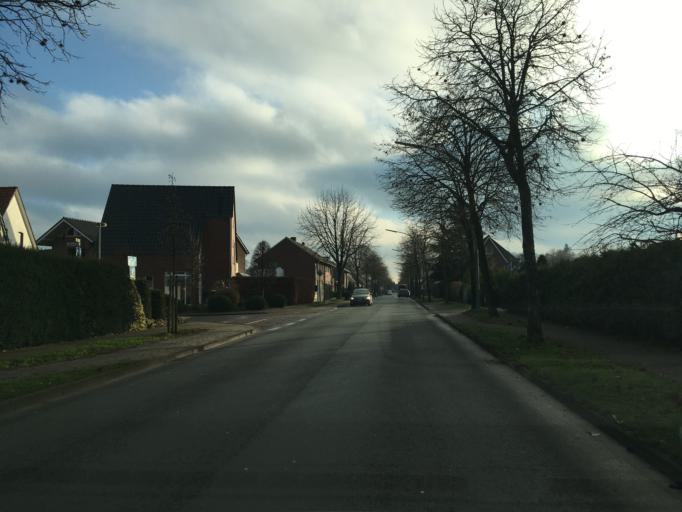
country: DE
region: North Rhine-Westphalia
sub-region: Regierungsbezirk Munster
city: Gescher
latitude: 51.9591
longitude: 6.9912
